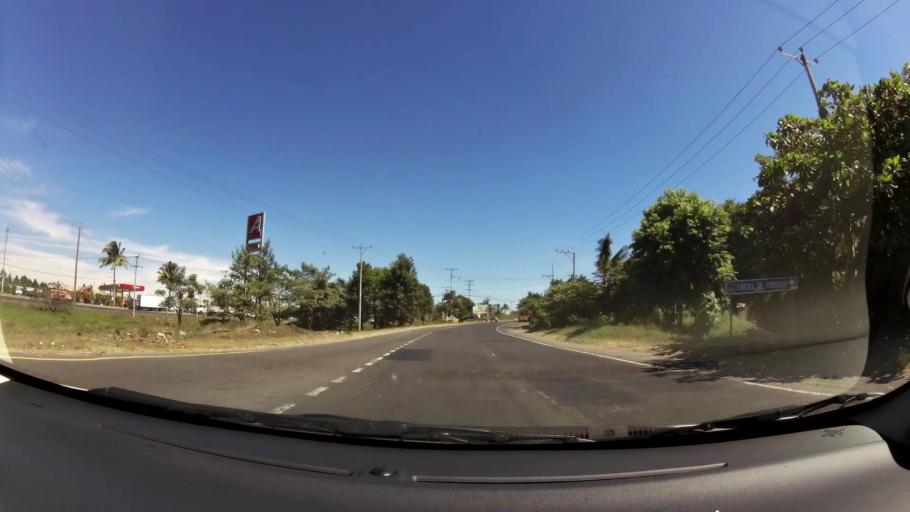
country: SV
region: La Libertad
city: San Juan Opico
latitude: 13.7875
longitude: -89.3584
